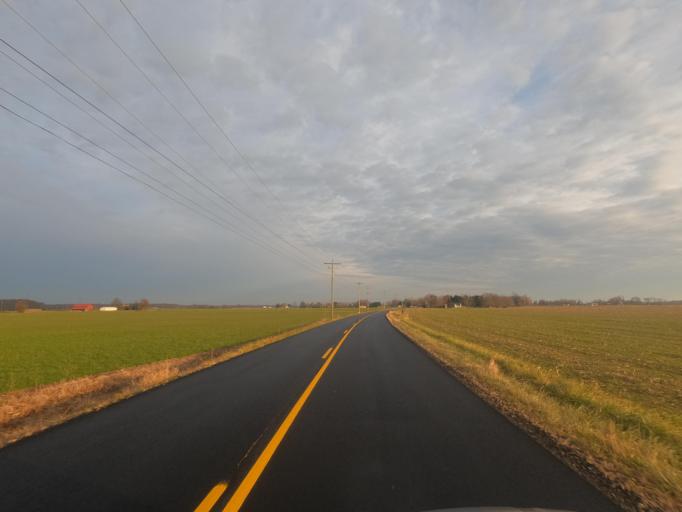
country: US
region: Delaware
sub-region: New Castle County
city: Townsend
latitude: 39.3019
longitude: -75.8296
